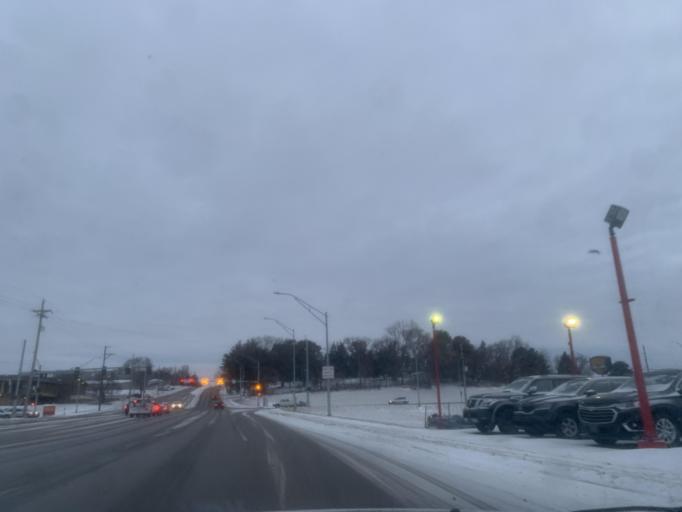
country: US
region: Nebraska
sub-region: Douglas County
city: Ralston
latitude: 41.2135
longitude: -96.0432
